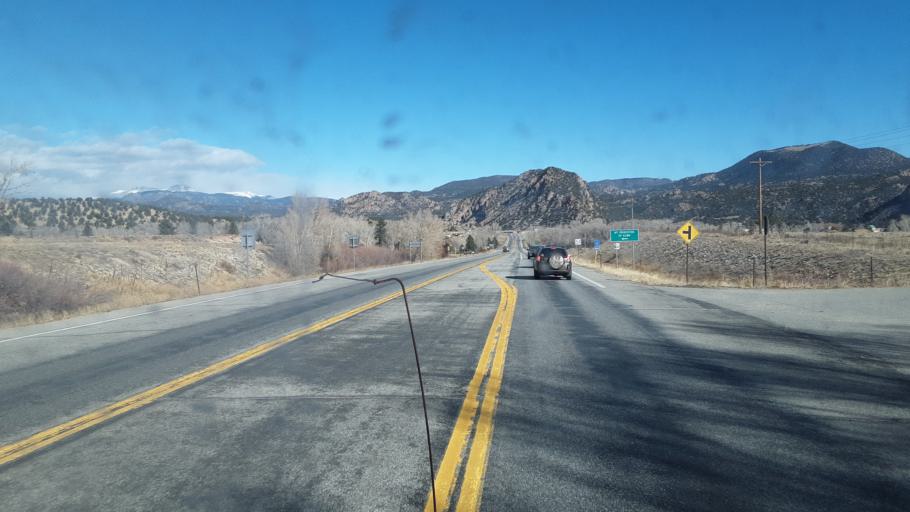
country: US
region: Colorado
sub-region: Chaffee County
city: Buena Vista
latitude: 38.7375
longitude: -106.0848
